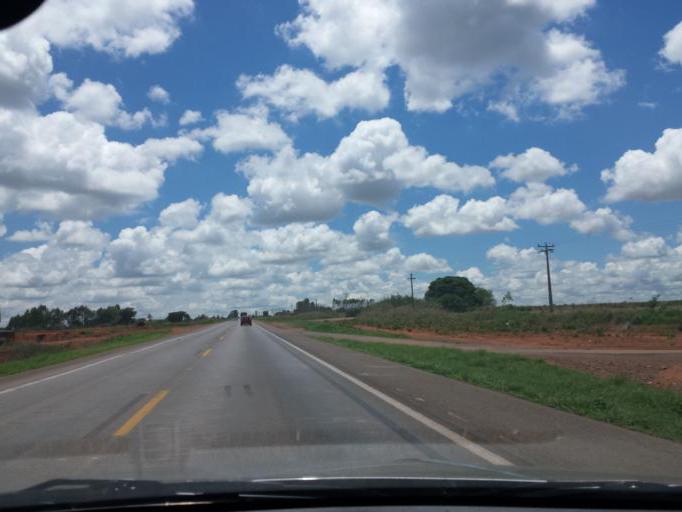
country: BR
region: Goias
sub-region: Cristalina
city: Cristalina
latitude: -16.7155
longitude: -47.6643
